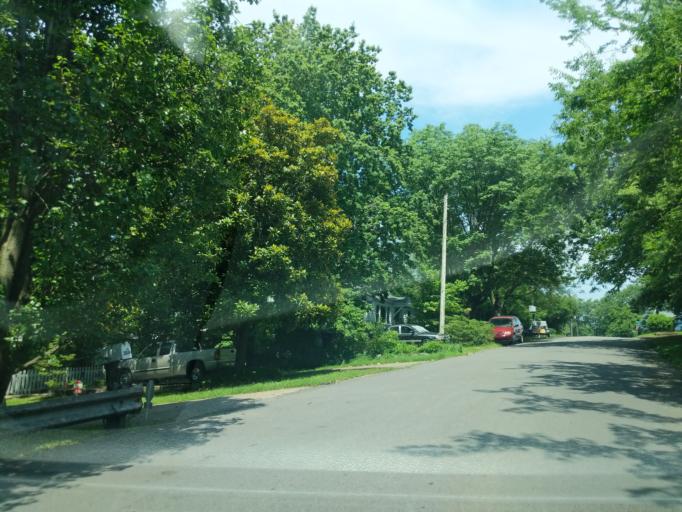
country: US
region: Tennessee
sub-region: Davidson County
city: Lakewood
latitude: 36.2543
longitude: -86.6441
